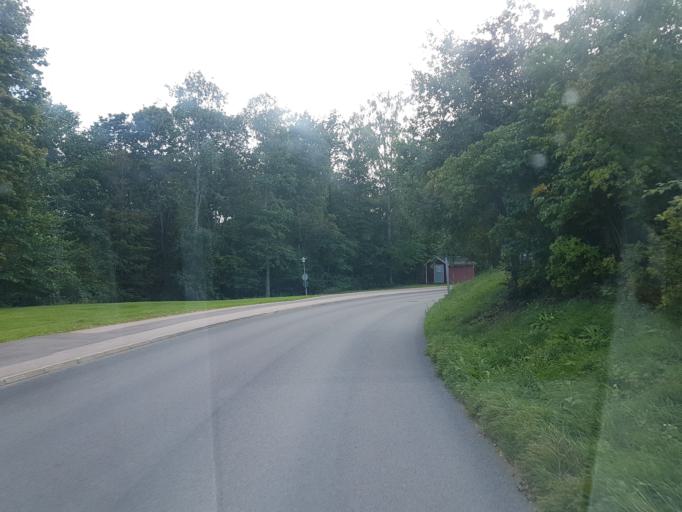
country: SE
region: Dalarna
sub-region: Saters Kommun
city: Saeter
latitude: 60.3496
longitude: 15.7519
